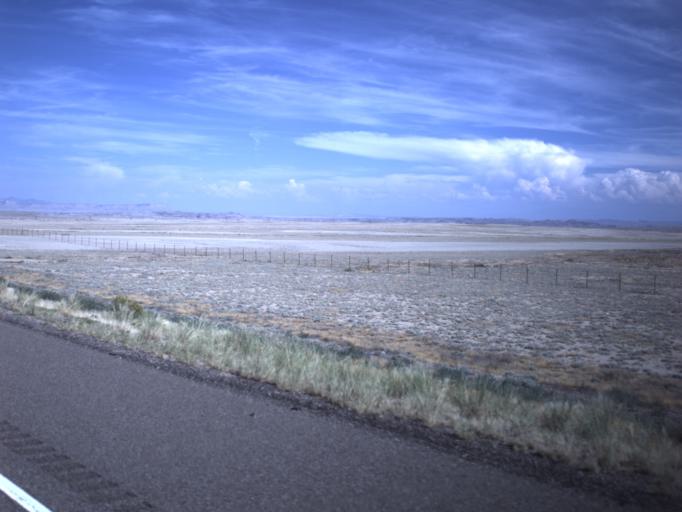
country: US
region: Utah
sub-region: Carbon County
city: East Carbon City
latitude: 38.9540
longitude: -110.3068
